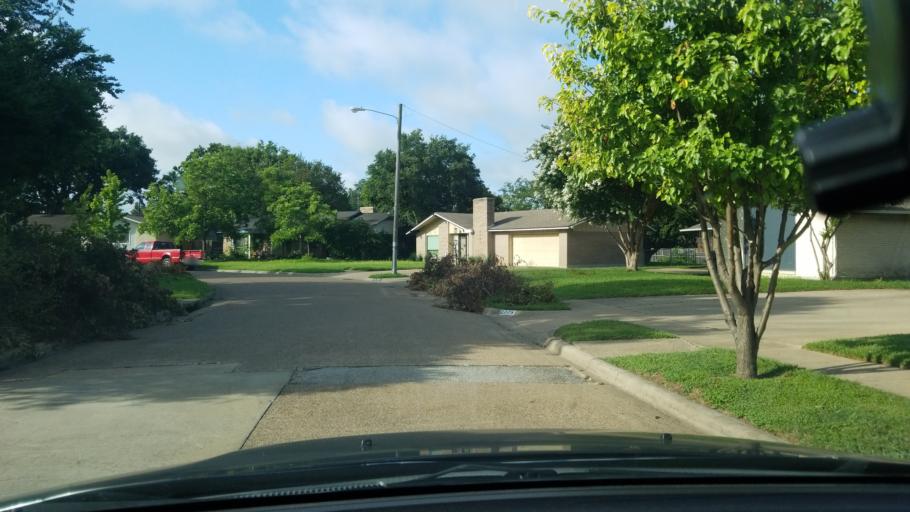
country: US
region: Texas
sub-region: Dallas County
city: Mesquite
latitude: 32.8162
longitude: -96.6861
